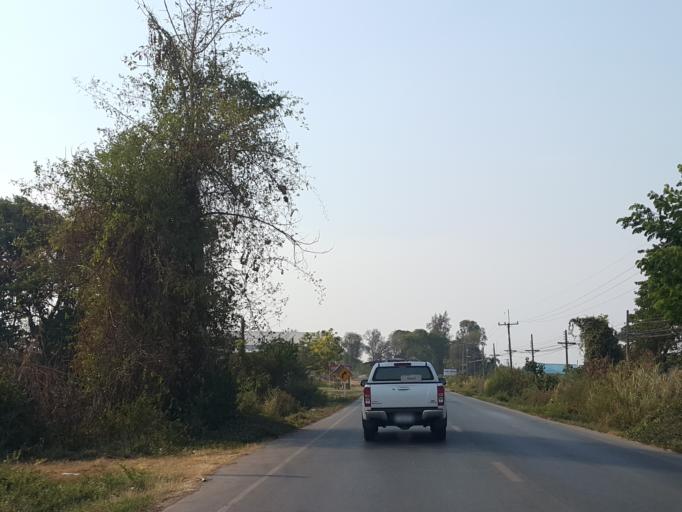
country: TH
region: Phitsanulok
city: Phrom Phiram
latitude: 17.0015
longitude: 100.2056
